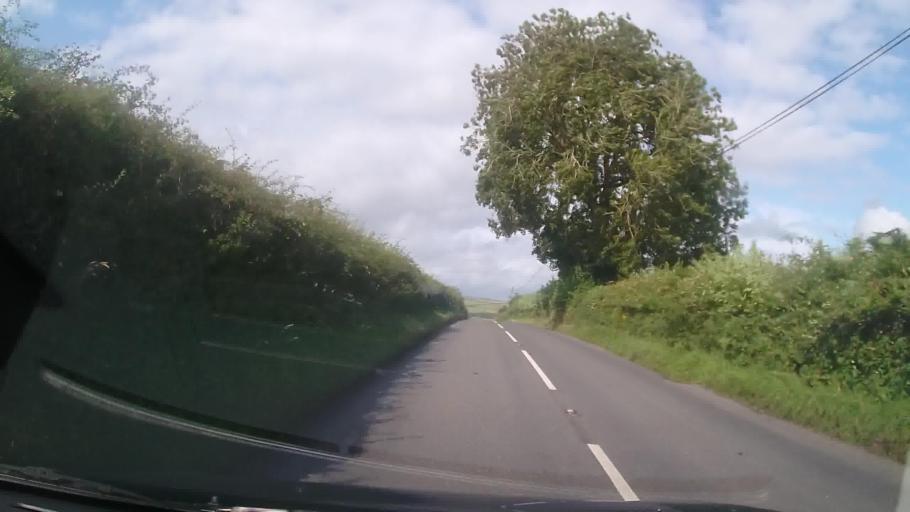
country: GB
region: Wales
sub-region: Sir Powys
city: Knighton
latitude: 52.3737
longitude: -3.0493
